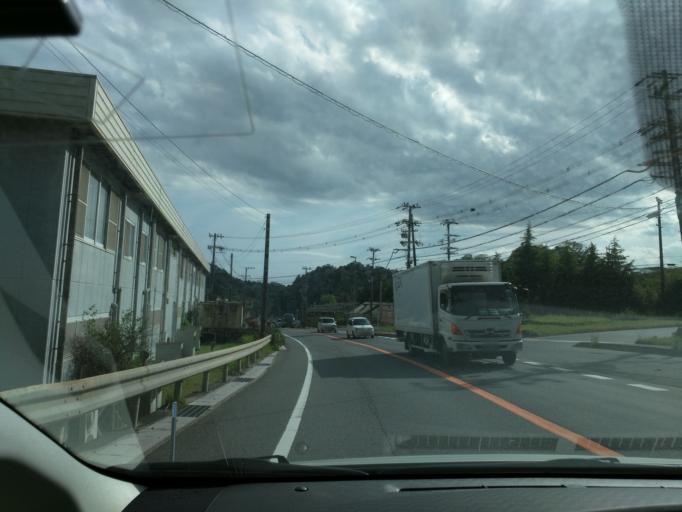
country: JP
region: Kyoto
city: Uji
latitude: 34.8371
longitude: 135.8278
